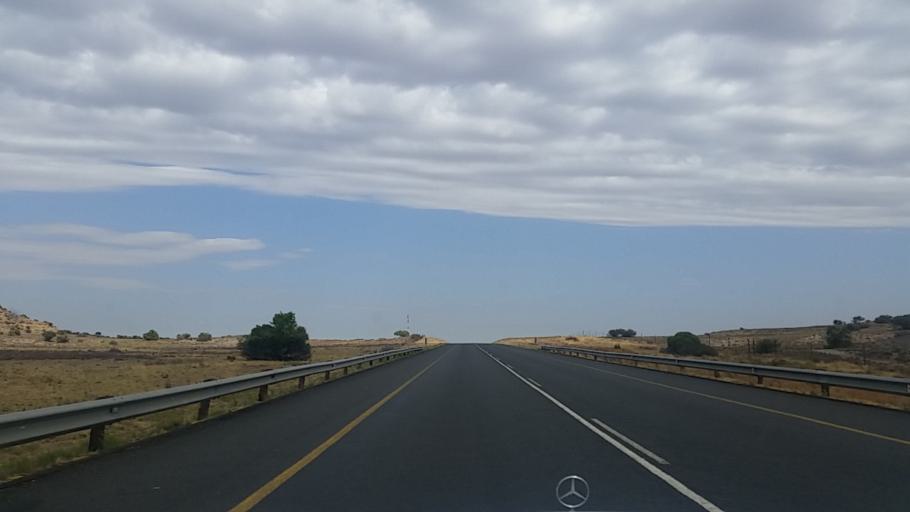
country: ZA
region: Northern Cape
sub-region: Pixley ka Seme District Municipality
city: Colesberg
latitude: -30.6184
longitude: 25.3179
